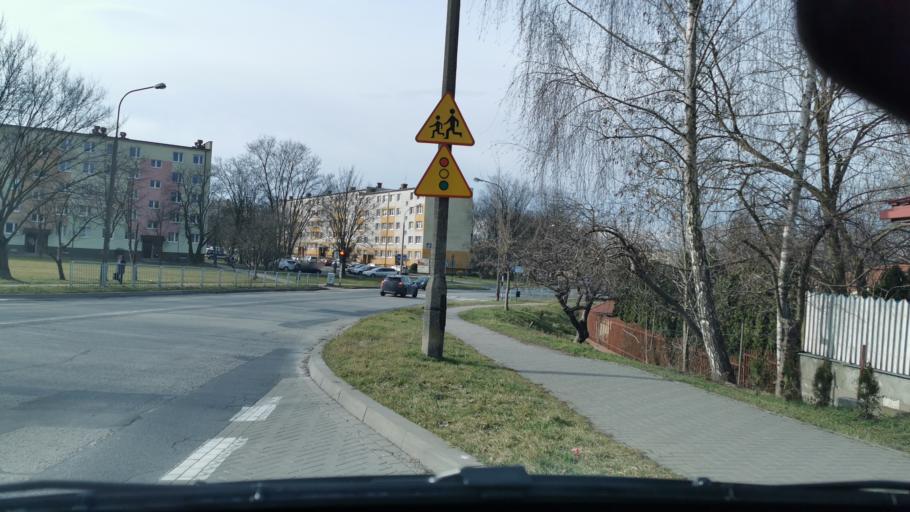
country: PL
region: Lublin Voivodeship
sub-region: Powiat lubelski
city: Lublin
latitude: 51.2146
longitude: 22.5452
